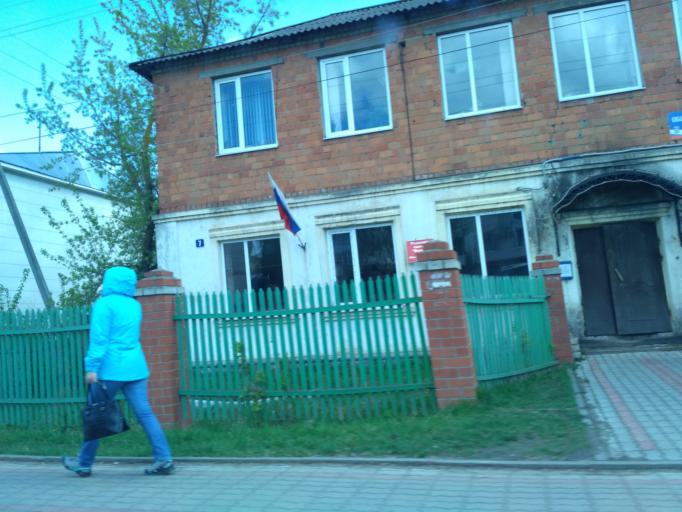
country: RU
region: Nizjnij Novgorod
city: Vad
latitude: 55.5322
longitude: 44.2121
